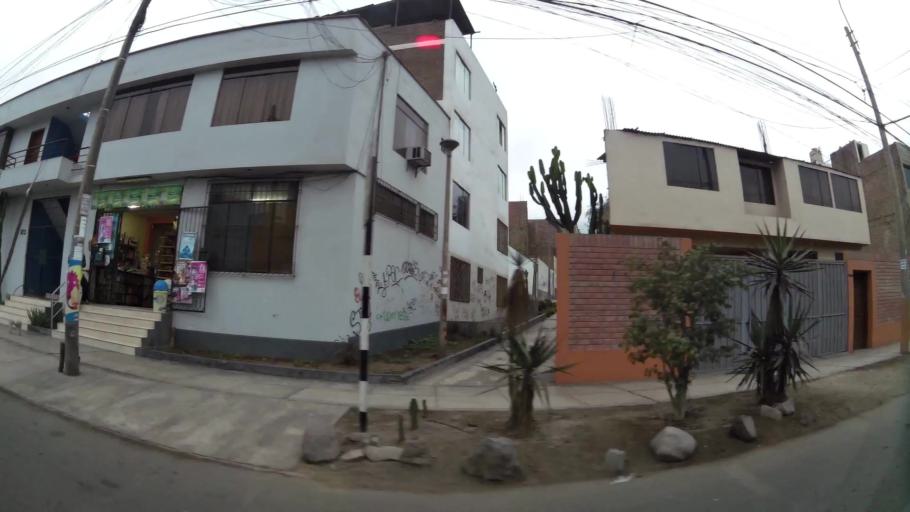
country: PE
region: Lima
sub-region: Lima
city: La Molina
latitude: -12.1109
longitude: -76.9386
